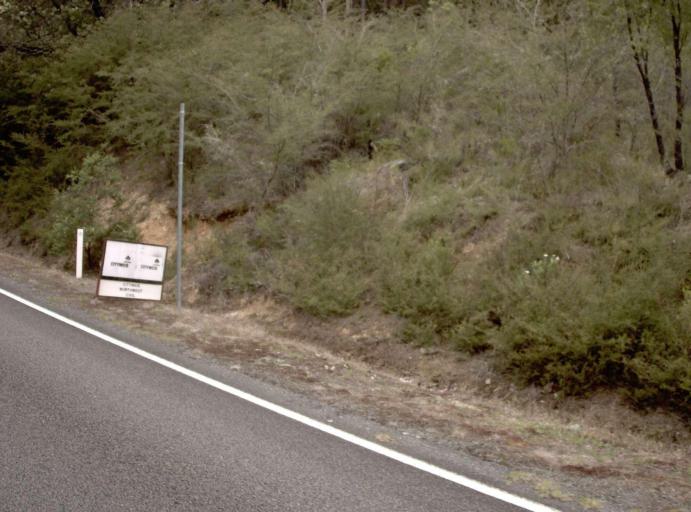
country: AU
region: New South Wales
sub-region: Bombala
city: Bombala
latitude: -37.2324
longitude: 149.2721
